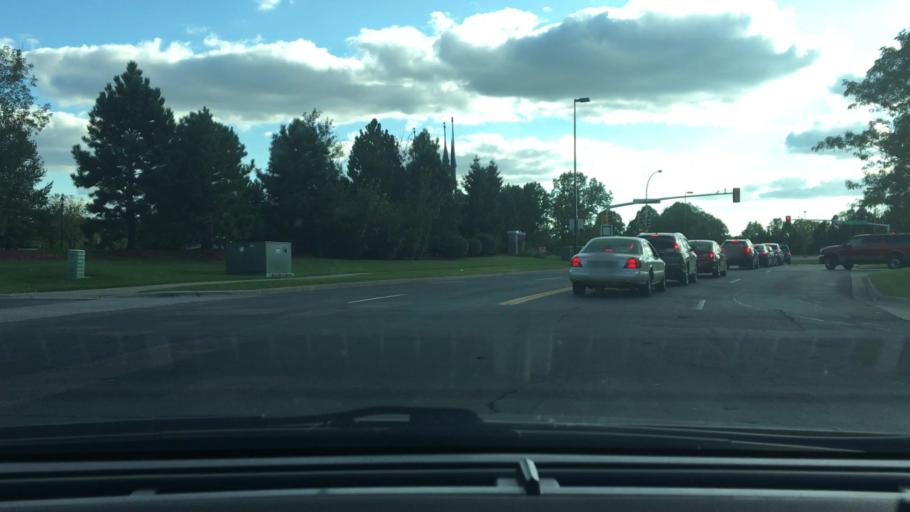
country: US
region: Minnesota
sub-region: Hennepin County
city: Maple Grove
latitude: 45.0649
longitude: -93.4397
